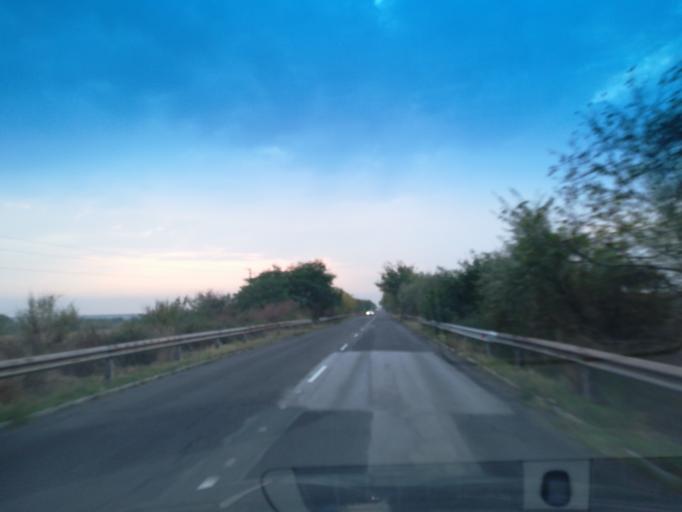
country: BG
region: Stara Zagora
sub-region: Obshtina Chirpan
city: Chirpan
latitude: 42.1902
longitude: 25.2859
